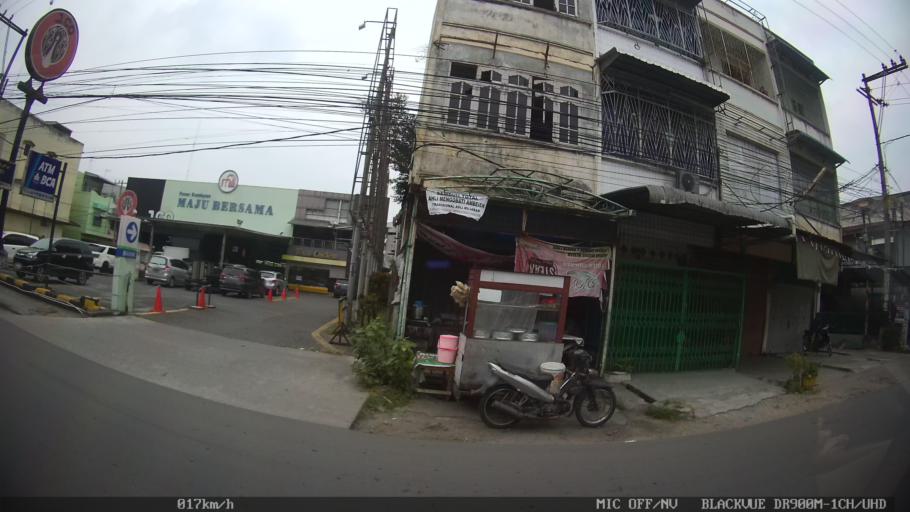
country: ID
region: North Sumatra
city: Deli Tua
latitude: 3.5416
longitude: 98.6857
